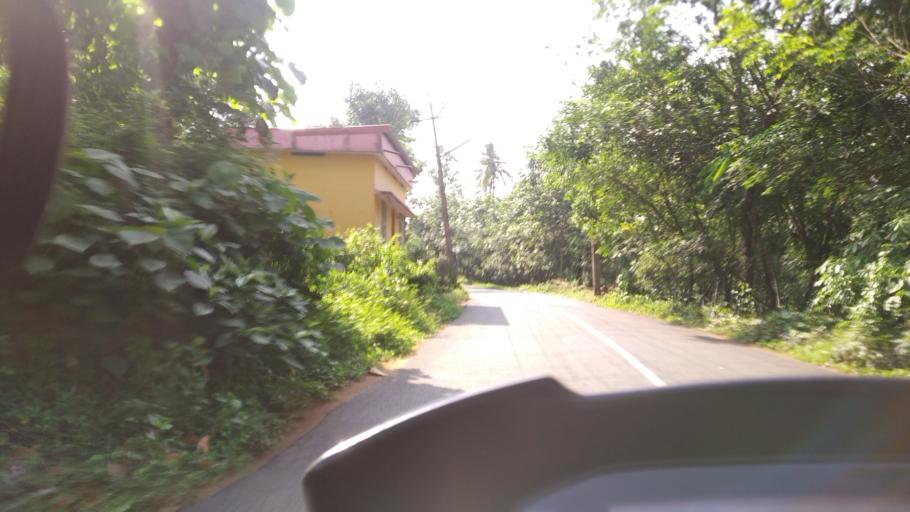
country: IN
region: Kerala
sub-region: Kottayam
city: Palackattumala
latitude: 9.8023
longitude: 76.5790
